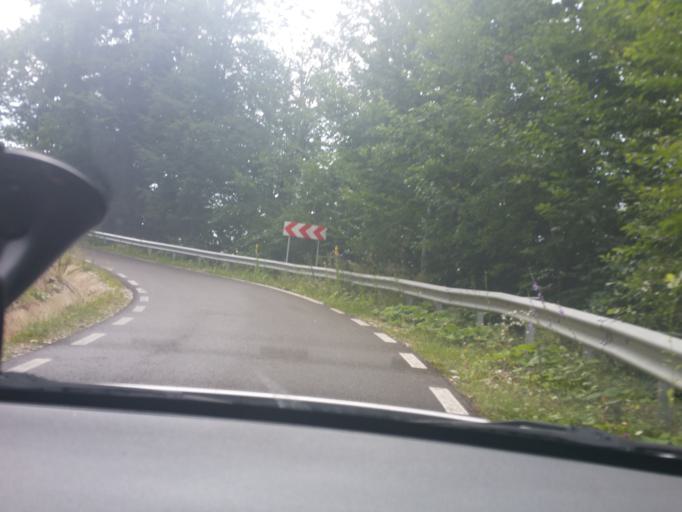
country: RO
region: Alba
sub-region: Comuna Garda de Sus
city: Garda de Sus
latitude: 46.4732
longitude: 22.8172
